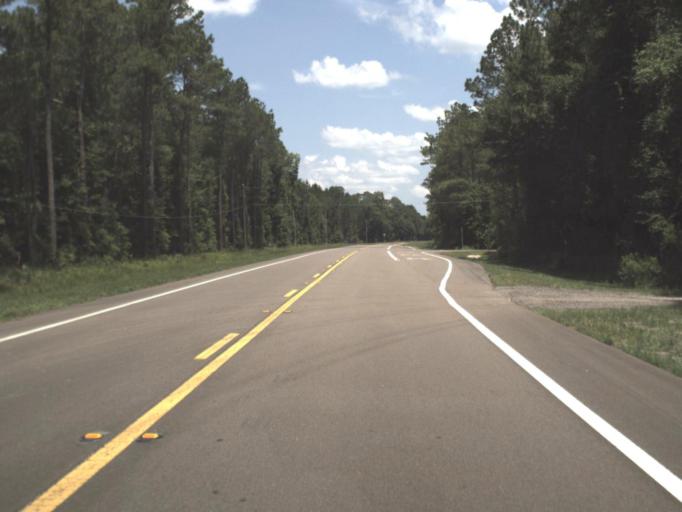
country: US
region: Florida
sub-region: Alachua County
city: Alachua
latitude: 29.7708
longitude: -82.3677
